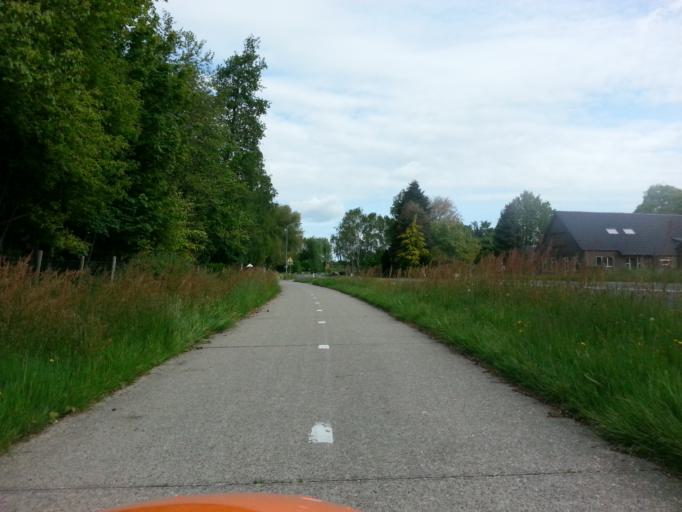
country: NL
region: Utrecht
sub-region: Gemeente Utrechtse Heuvelrug
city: Overberg
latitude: 52.0954
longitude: 5.5135
